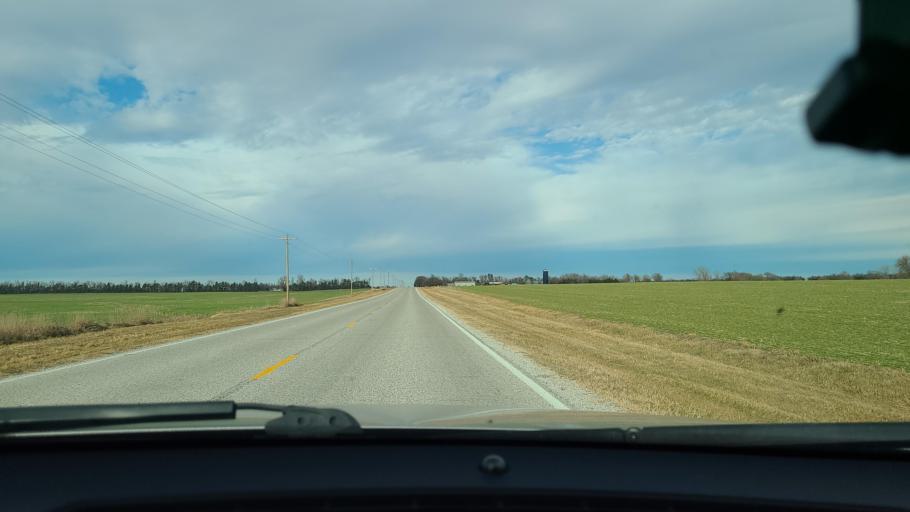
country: US
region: Kansas
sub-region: McPherson County
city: Inman
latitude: 38.3068
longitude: -97.9248
